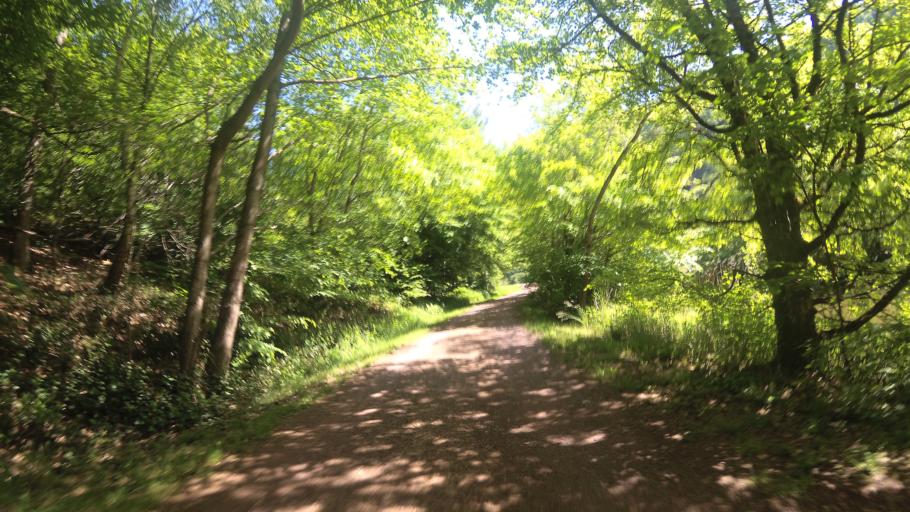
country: DE
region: Saarland
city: Orscholz
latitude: 49.4994
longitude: 6.5562
